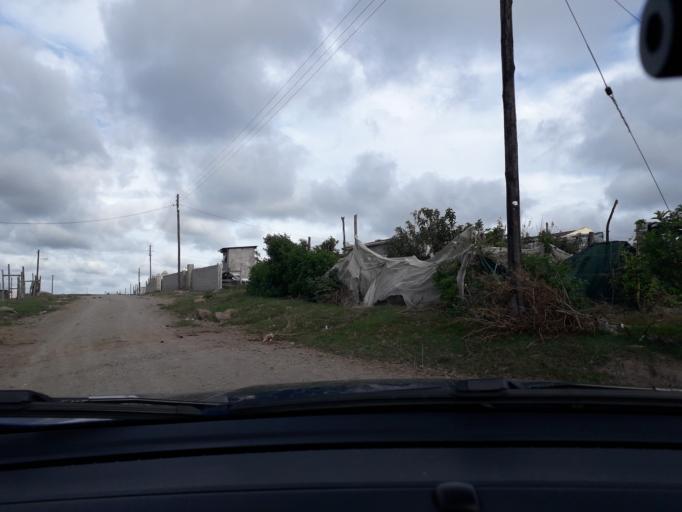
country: ZA
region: Eastern Cape
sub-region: Buffalo City Metropolitan Municipality
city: East London
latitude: -32.8508
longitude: 27.9845
